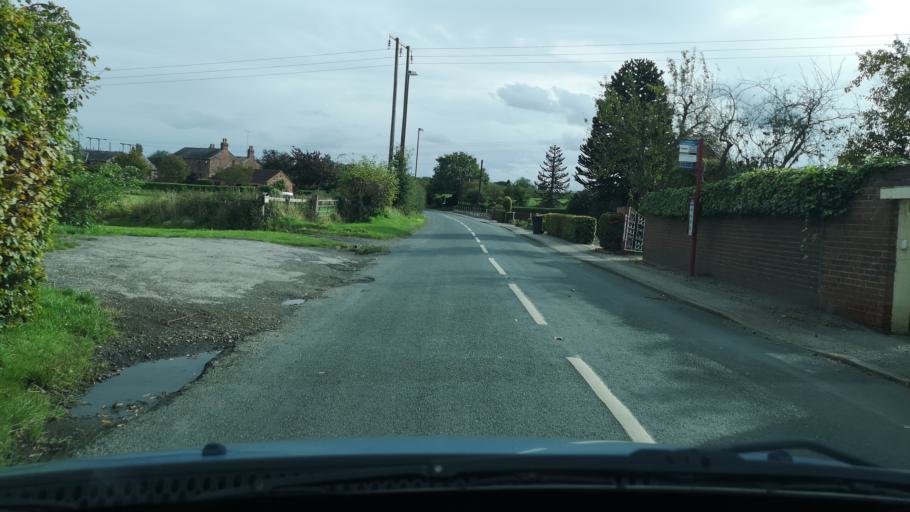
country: GB
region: England
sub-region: City and Borough of Wakefield
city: Normanton
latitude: 53.6881
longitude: -1.3933
